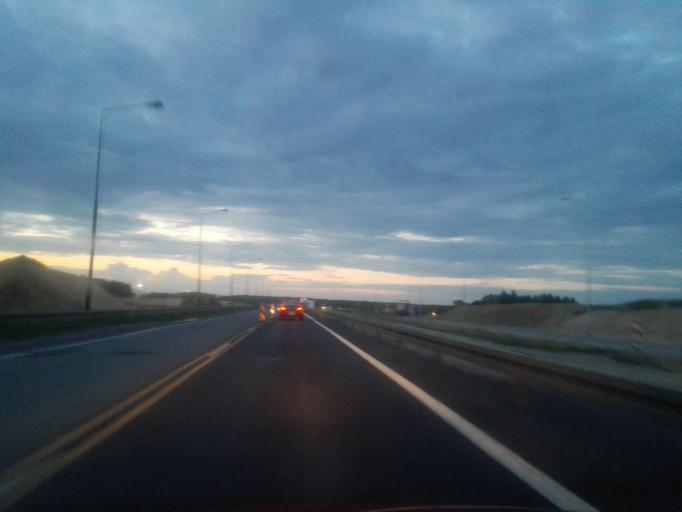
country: PL
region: Lodz Voivodeship
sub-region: Powiat piotrkowski
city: Czarnocin
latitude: 51.5431
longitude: 19.6027
